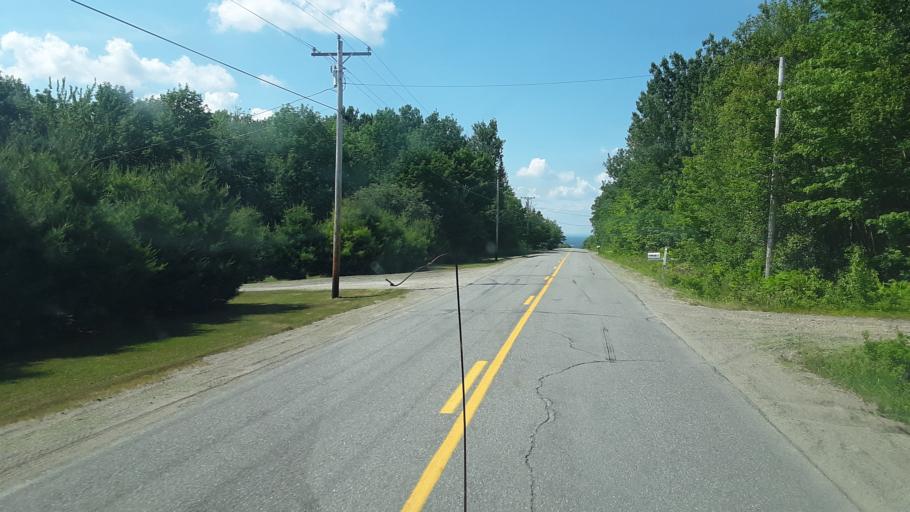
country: US
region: Maine
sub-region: Washington County
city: Calais
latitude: 45.0911
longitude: -67.5052
